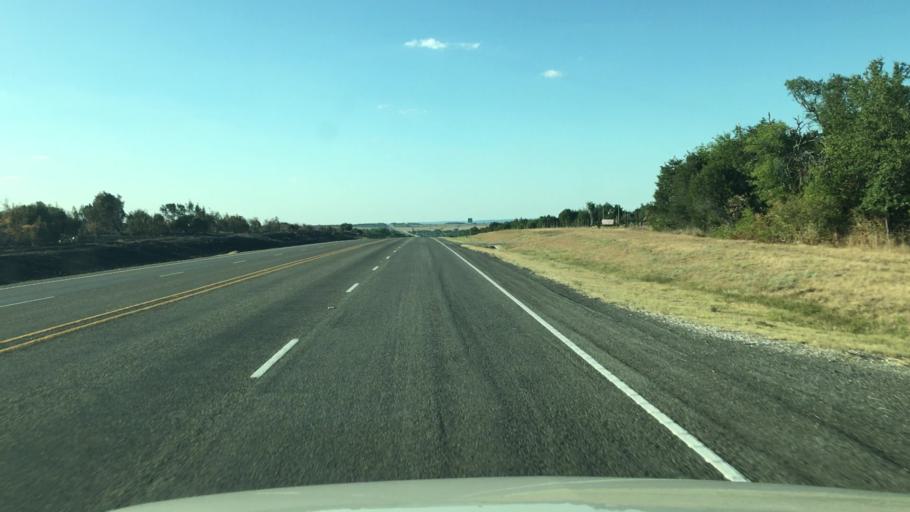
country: US
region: Texas
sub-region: Lampasas County
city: Lampasas
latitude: 31.1927
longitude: -98.1718
